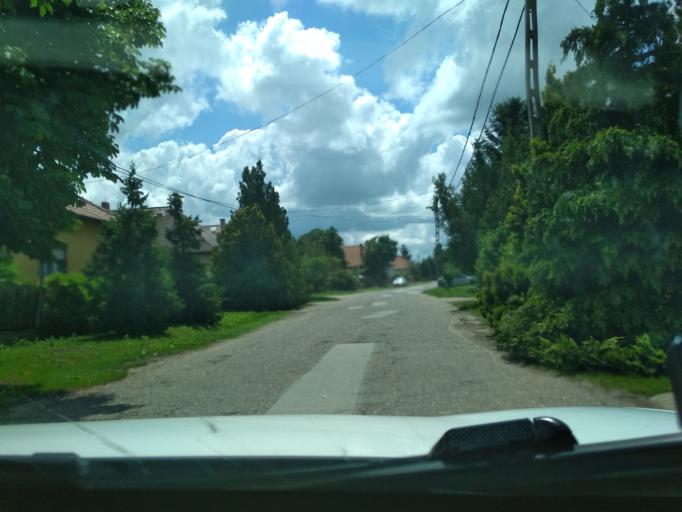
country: HU
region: Jasz-Nagykun-Szolnok
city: Tiszafured
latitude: 47.6068
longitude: 20.7749
